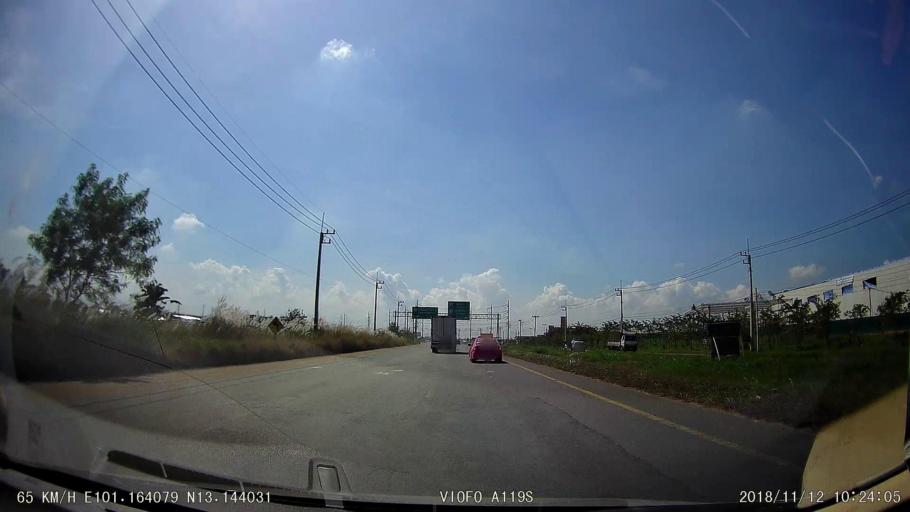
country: TH
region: Chon Buri
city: Ban Bueng
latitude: 13.1437
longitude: 101.1641
